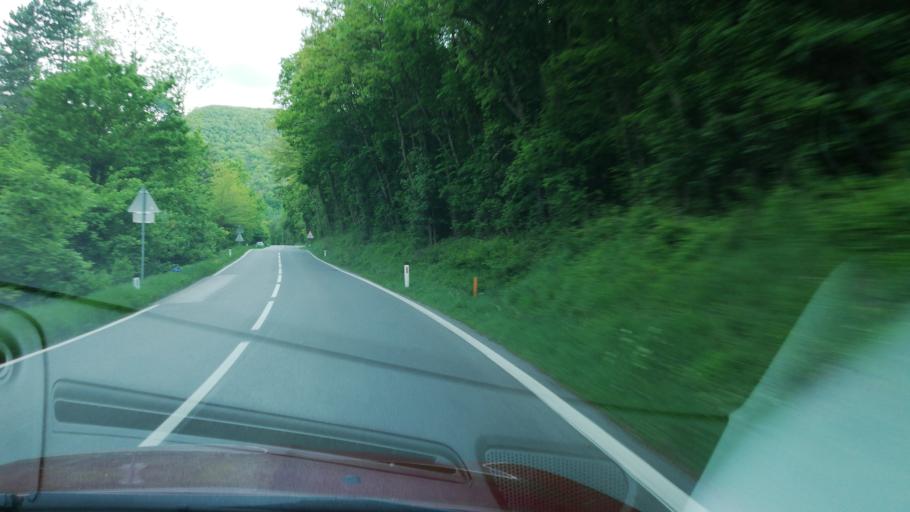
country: AT
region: Lower Austria
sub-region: Politischer Bezirk Modling
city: Gaaden
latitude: 48.0186
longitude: 16.1888
